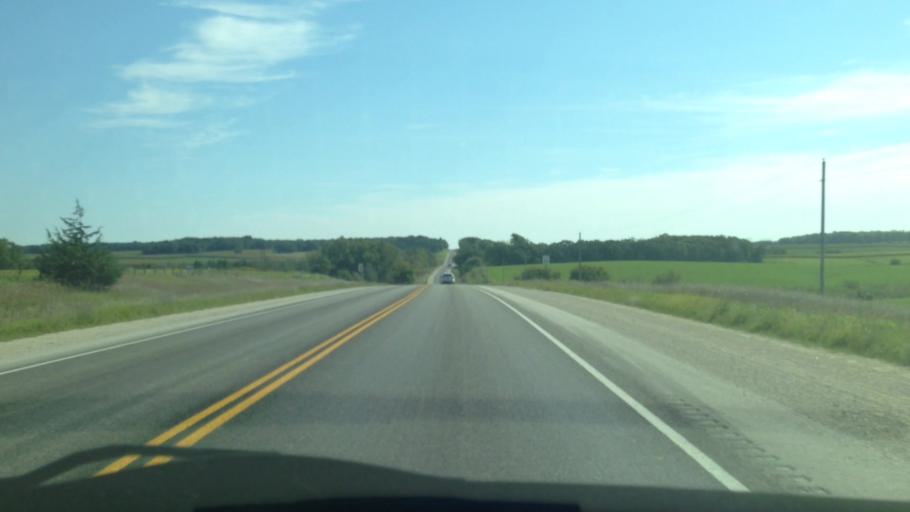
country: US
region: Minnesota
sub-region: Fillmore County
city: Harmony
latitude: 43.5149
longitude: -91.8671
